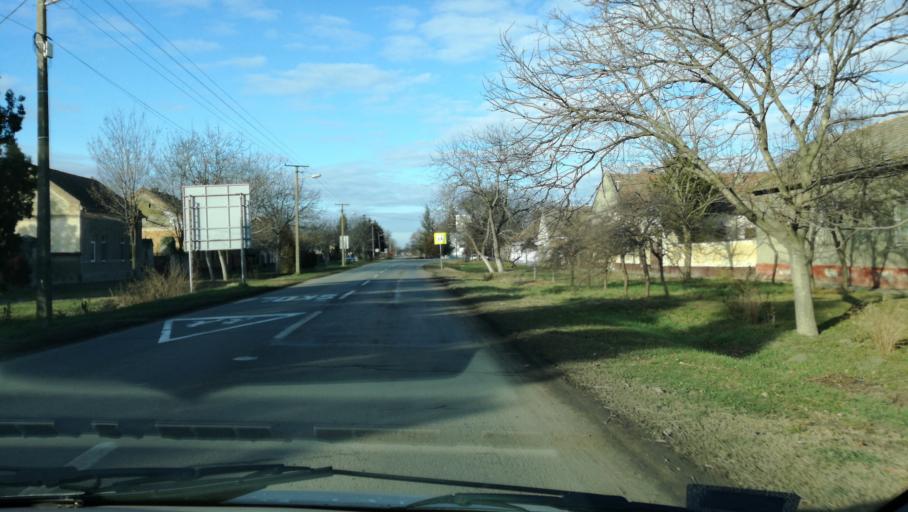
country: RS
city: Ostojicevo
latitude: 45.8901
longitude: 20.1664
